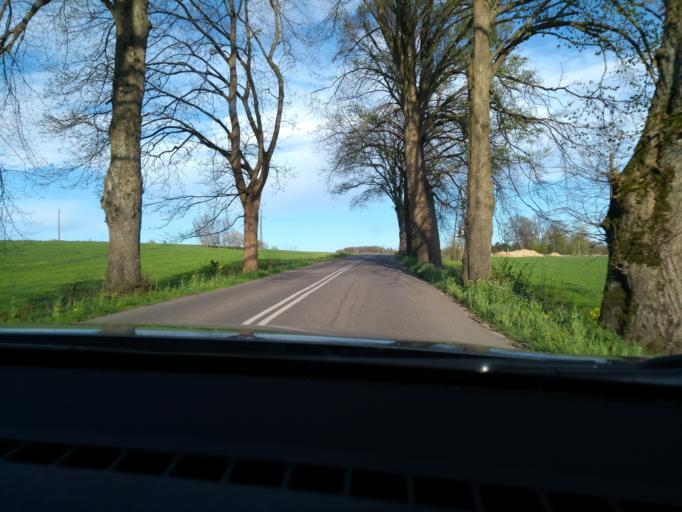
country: PL
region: Pomeranian Voivodeship
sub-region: Powiat leborski
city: Cewice
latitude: 54.3402
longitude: 17.7540
